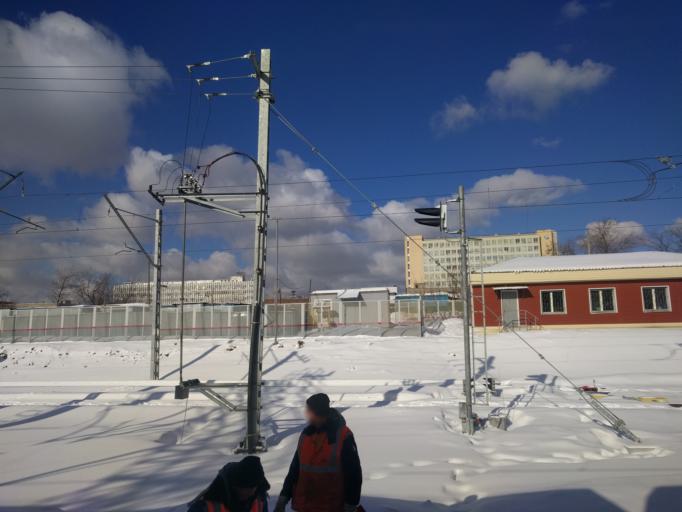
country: RU
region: Moscow
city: Ryazanskiy
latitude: 55.7446
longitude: 37.7356
